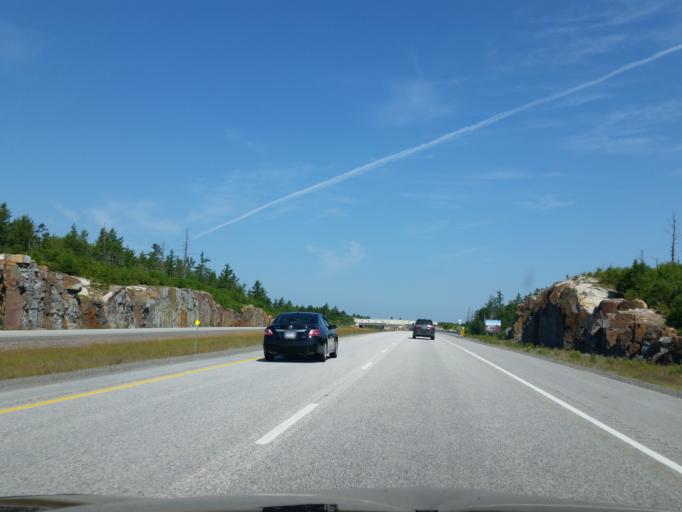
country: CA
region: Ontario
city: Greater Sudbury
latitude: 46.2339
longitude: -80.7777
